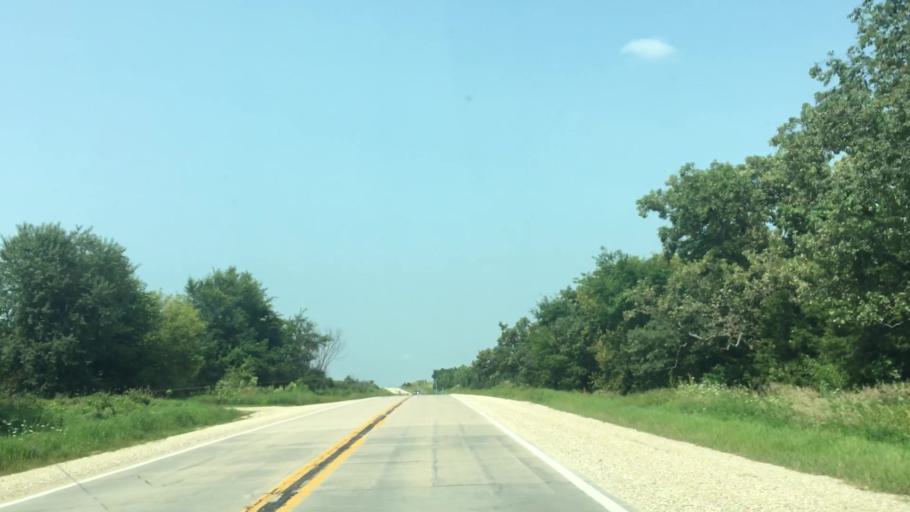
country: US
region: Iowa
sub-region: Fayette County
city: West Union
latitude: 43.1237
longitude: -91.8696
